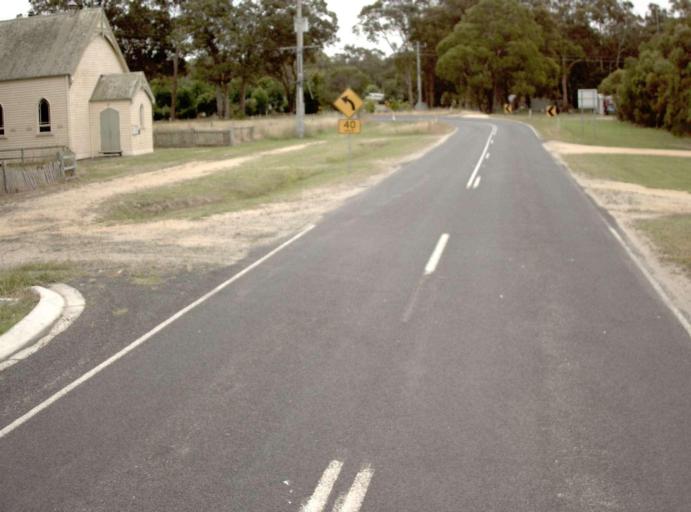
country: AU
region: Victoria
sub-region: Wellington
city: Sale
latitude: -38.5261
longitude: 146.8770
